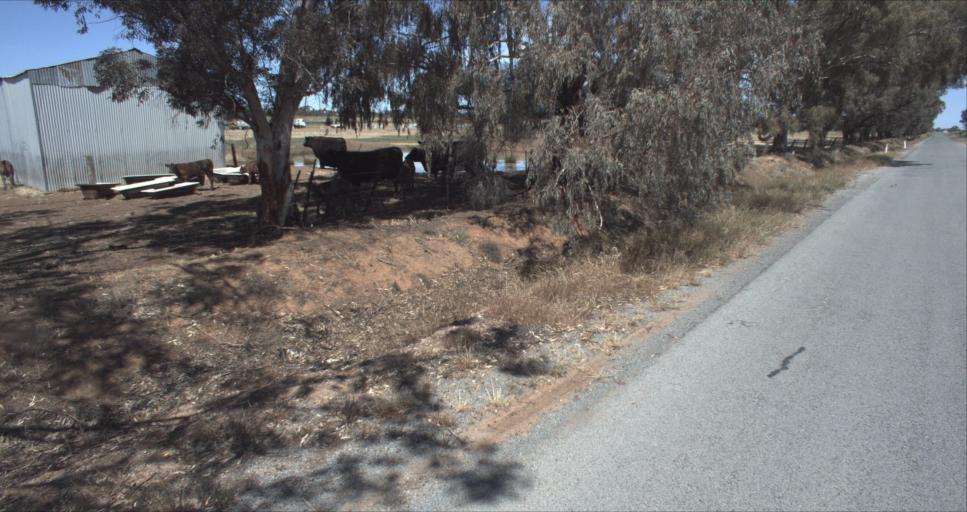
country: AU
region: New South Wales
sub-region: Leeton
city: Leeton
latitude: -34.5787
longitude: 146.4209
